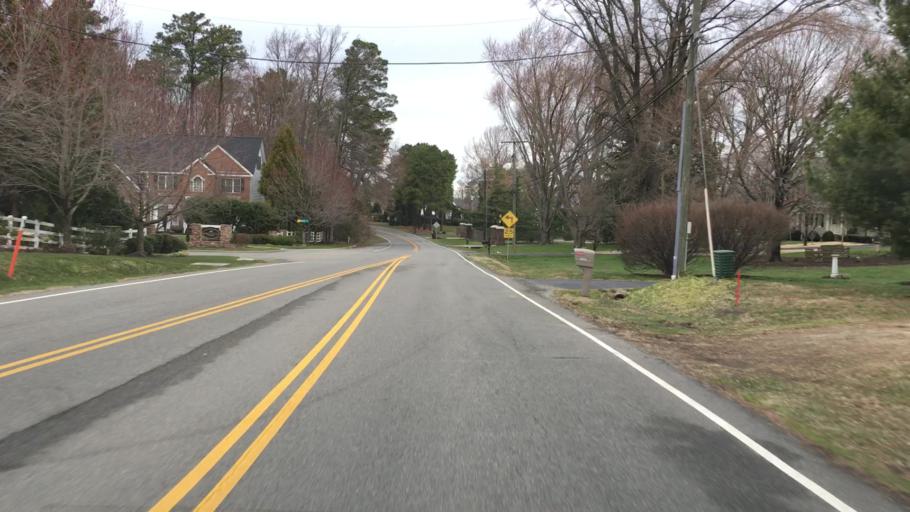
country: US
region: Virginia
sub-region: Henrico County
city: Glen Allen
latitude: 37.6723
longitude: -77.5420
